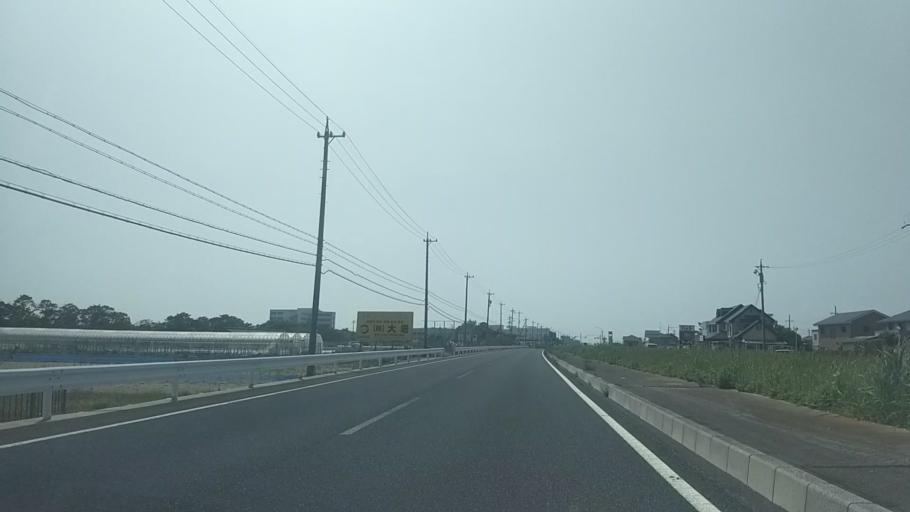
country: JP
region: Shizuoka
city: Hamamatsu
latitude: 34.6702
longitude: 137.7205
